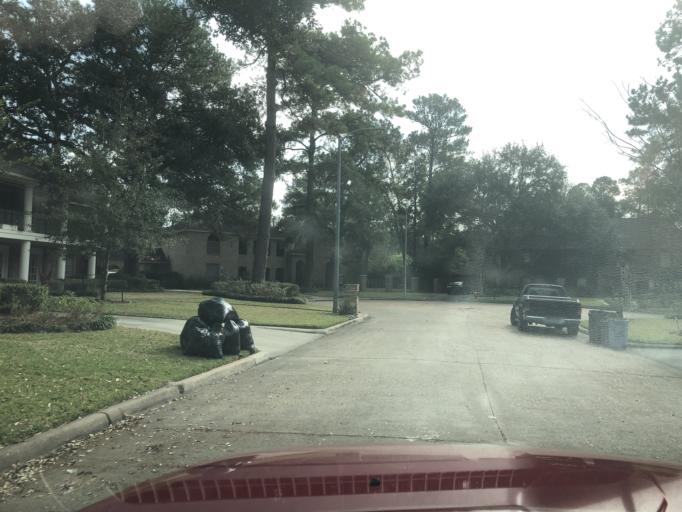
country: US
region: Texas
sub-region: Harris County
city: Spring
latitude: 30.0167
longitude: -95.4632
